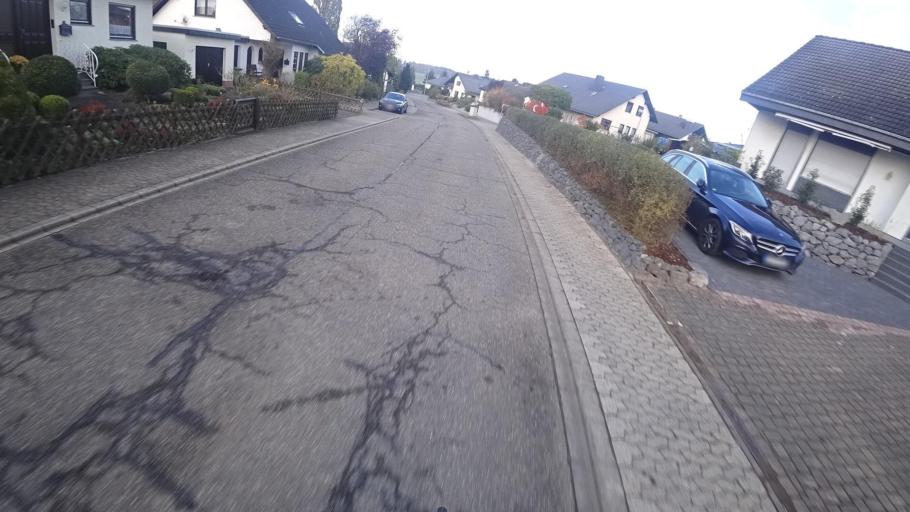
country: DE
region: Rheinland-Pfalz
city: Schwall
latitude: 50.1524
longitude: 7.5429
